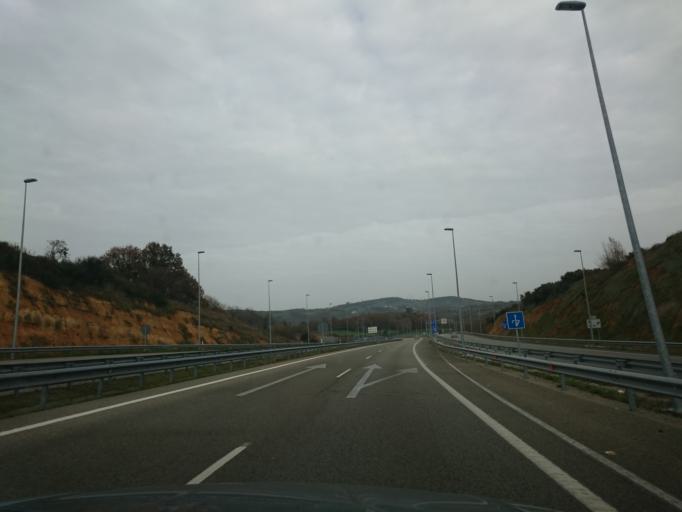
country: ES
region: Asturias
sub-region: Province of Asturias
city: Norena
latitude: 43.3926
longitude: -5.6868
